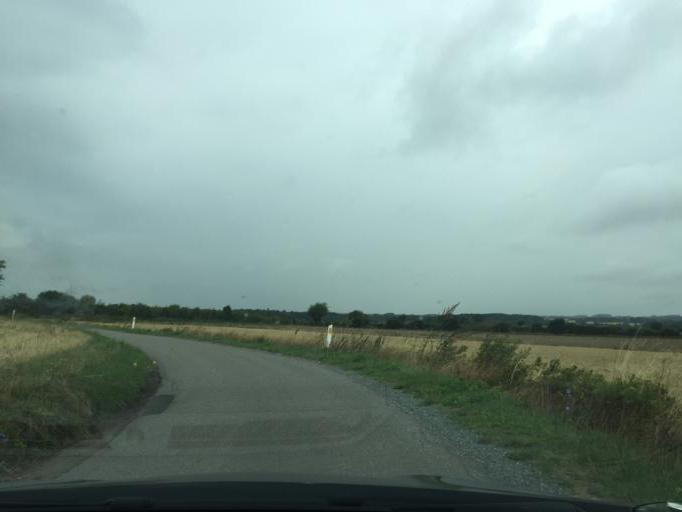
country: DK
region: South Denmark
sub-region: Assens Kommune
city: Harby
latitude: 55.2067
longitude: 10.0176
